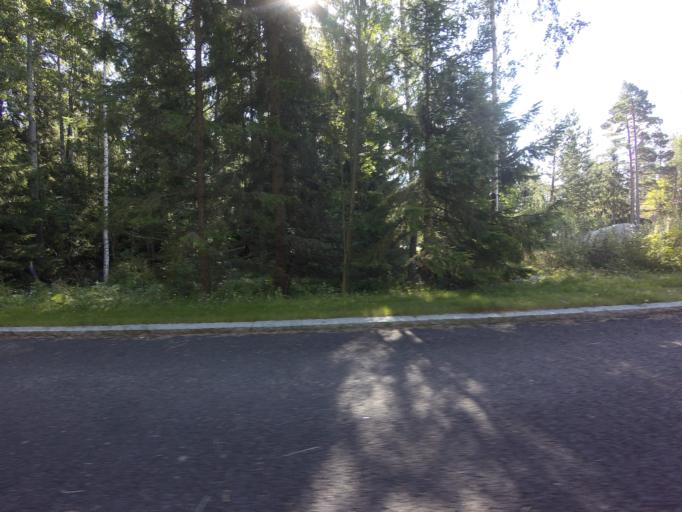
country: FI
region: Uusimaa
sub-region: Helsinki
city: Espoo
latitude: 60.1469
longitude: 24.5876
